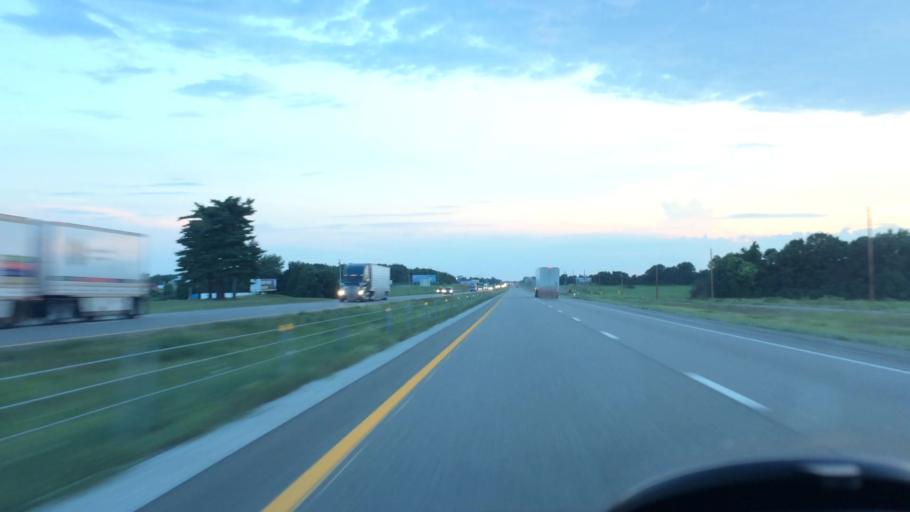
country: US
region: Missouri
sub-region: Greene County
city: Strafford
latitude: 37.2617
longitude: -93.1500
